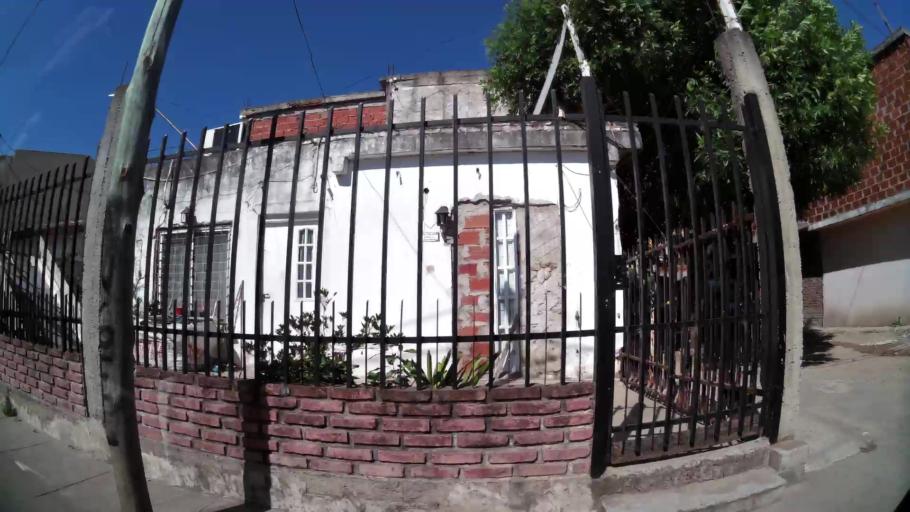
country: AR
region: Buenos Aires F.D.
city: Villa Lugano
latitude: -34.7063
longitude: -58.4739
